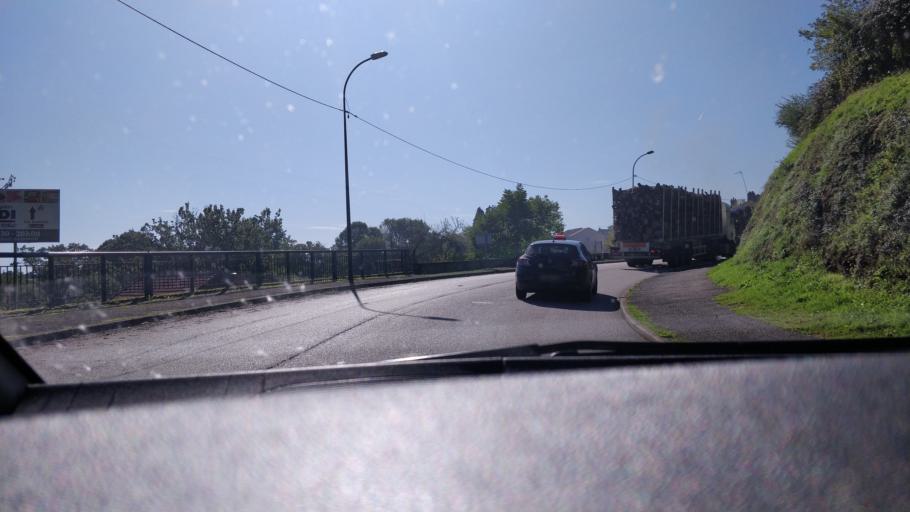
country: FR
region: Limousin
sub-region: Departement de la Haute-Vienne
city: Saint-Leonard-de-Noblat
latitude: 45.8421
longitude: 1.4936
